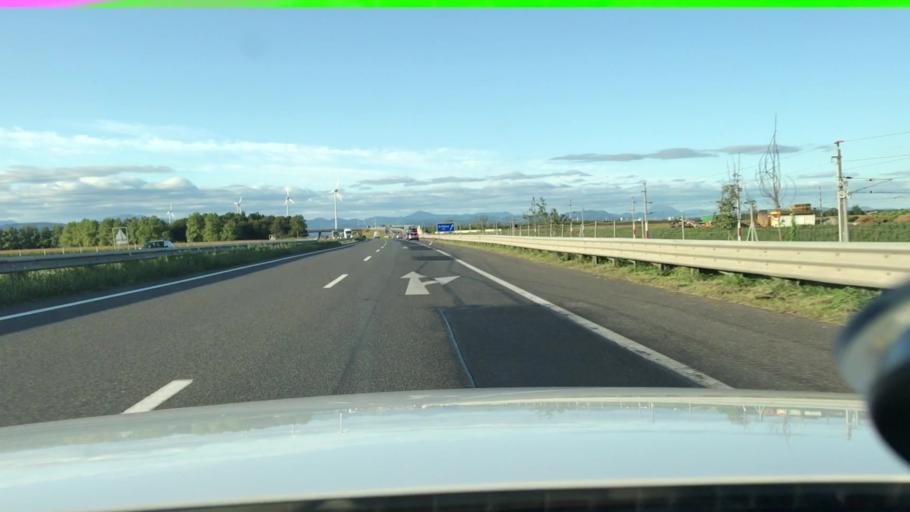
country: AT
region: Lower Austria
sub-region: Sankt Polten Stadt
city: Sankt Poelten
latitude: 48.2050
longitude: 15.6647
